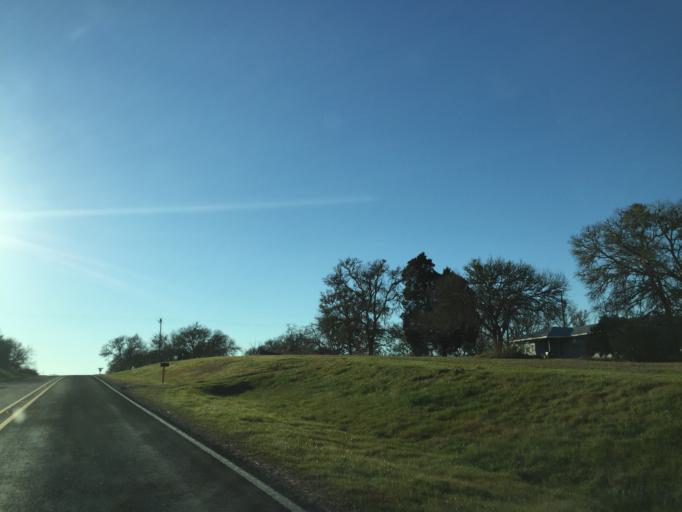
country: US
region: Texas
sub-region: Bastrop County
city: Elgin
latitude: 30.3625
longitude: -97.3231
